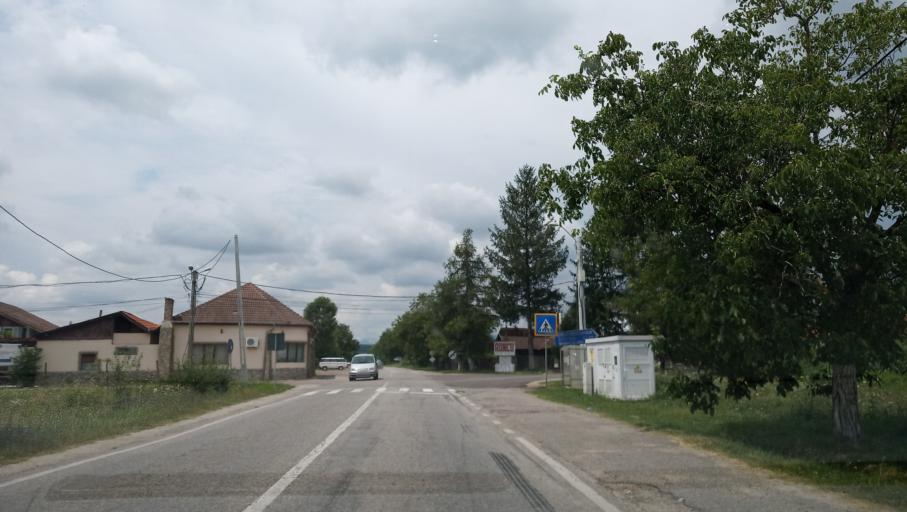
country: RO
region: Gorj
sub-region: Comuna Arcani
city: Arcani
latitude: 45.0879
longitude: 23.1530
